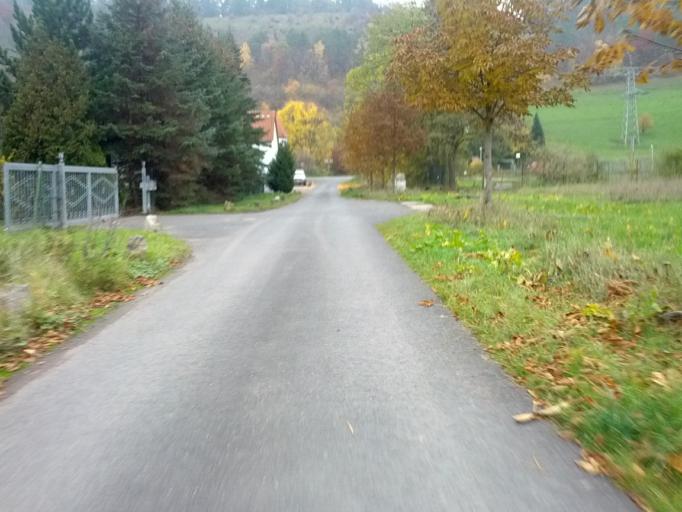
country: DE
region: Thuringia
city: Eisenach
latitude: 50.9662
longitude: 10.3622
